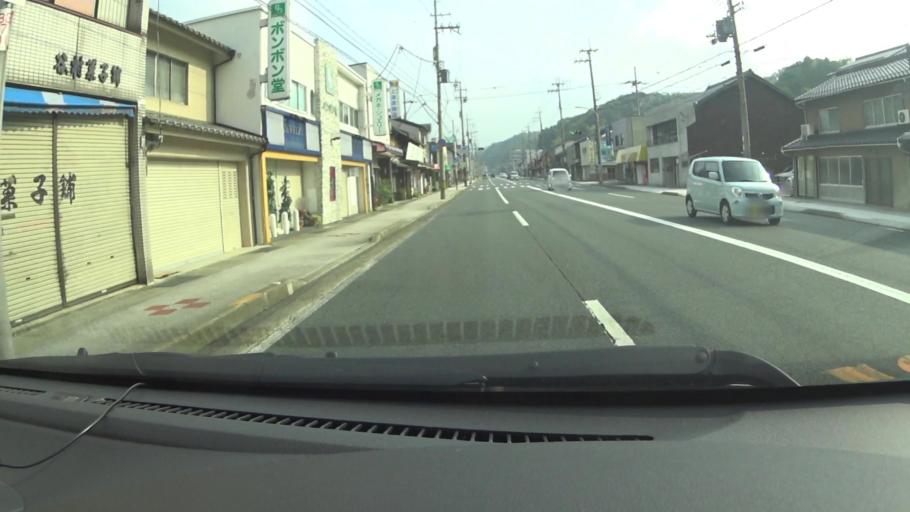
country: JP
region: Kyoto
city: Maizuru
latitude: 35.4744
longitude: 135.3671
